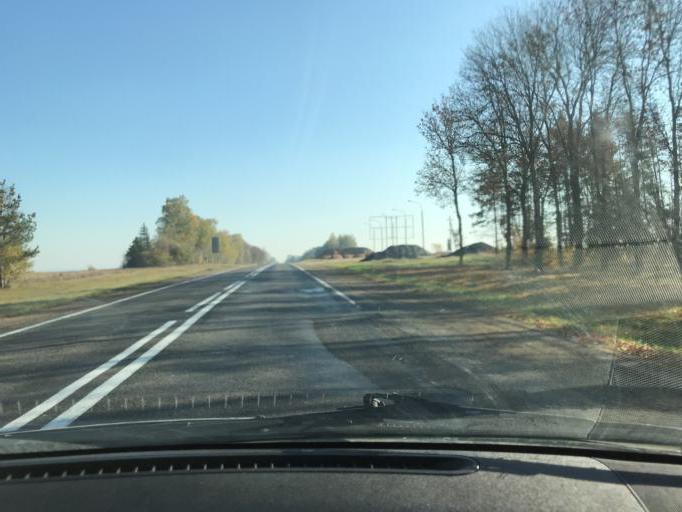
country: BY
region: Minsk
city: Klyetsk
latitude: 52.9639
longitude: 26.4896
